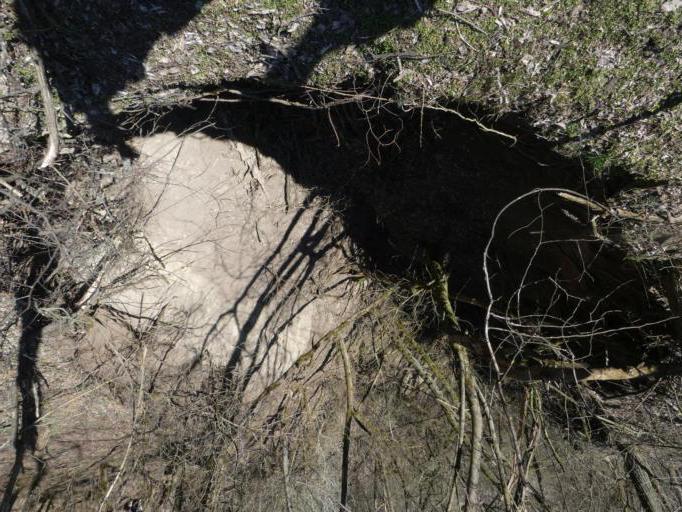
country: HU
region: Pest
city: Pecel
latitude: 47.5112
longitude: 19.3387
